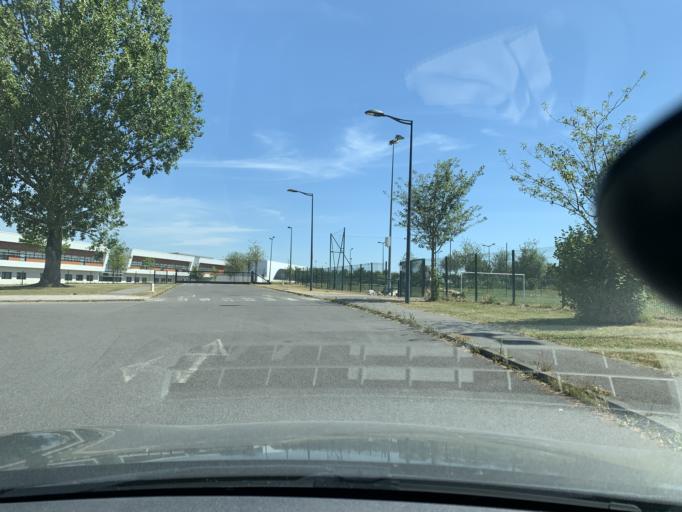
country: FR
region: Nord-Pas-de-Calais
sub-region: Departement du Nord
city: Cambrai
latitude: 50.1594
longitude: 3.2642
